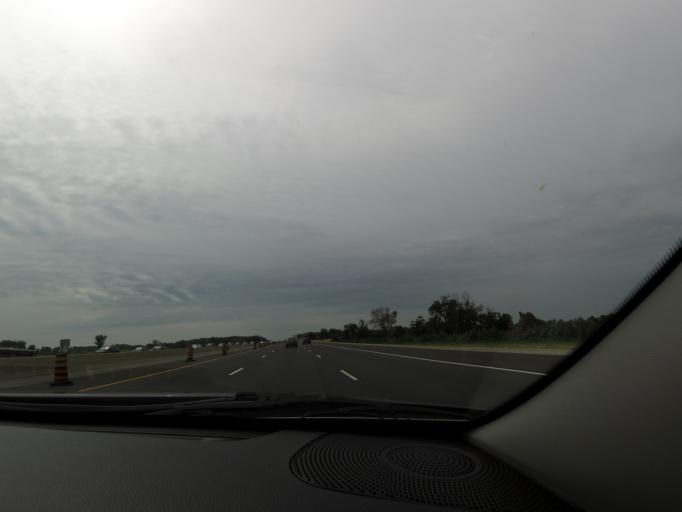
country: CA
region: Ontario
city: Bradford West Gwillimbury
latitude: 44.0180
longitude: -79.5914
